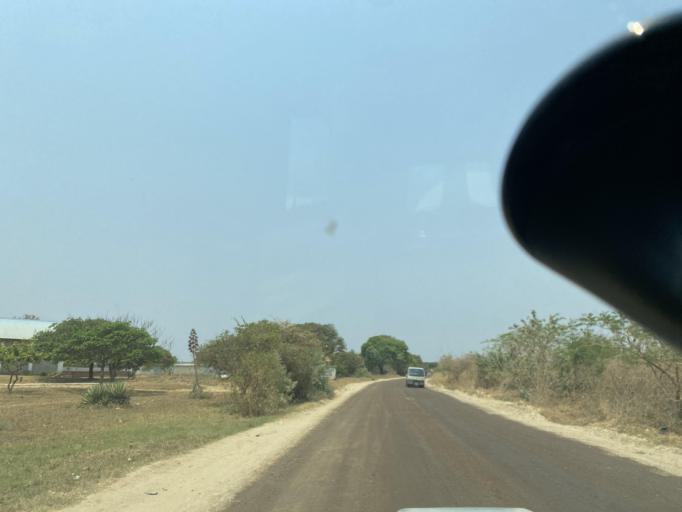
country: ZM
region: Lusaka
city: Lusaka
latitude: -15.5495
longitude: 28.3621
